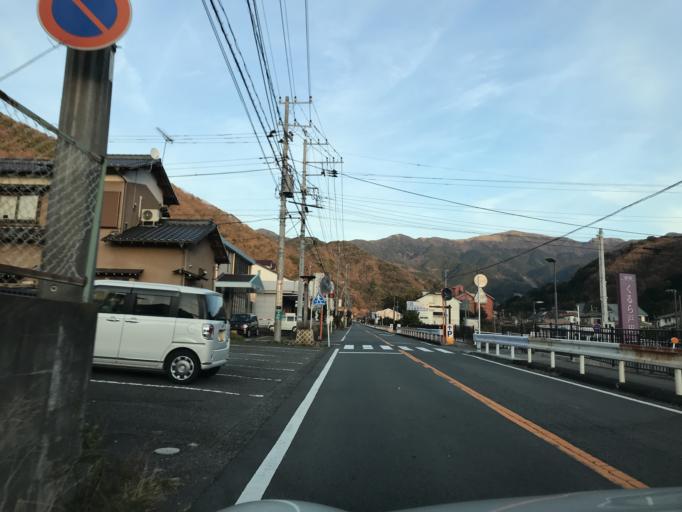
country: JP
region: Shizuoka
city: Heda
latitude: 34.9718
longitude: 138.7865
